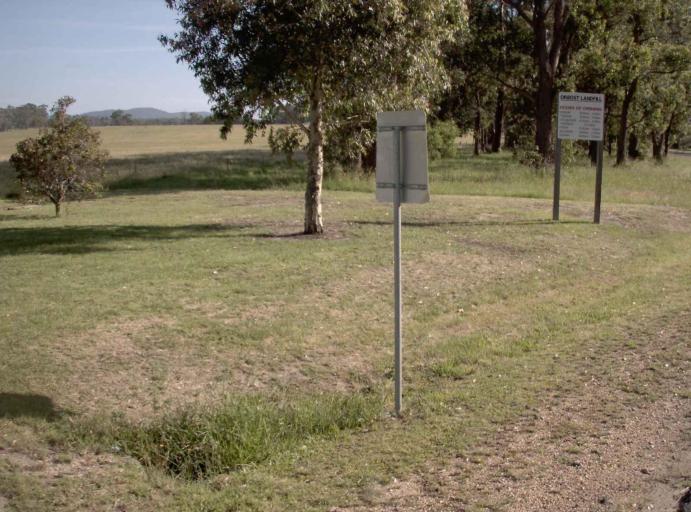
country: AU
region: Victoria
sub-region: East Gippsland
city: Lakes Entrance
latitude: -37.6973
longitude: 148.4642
